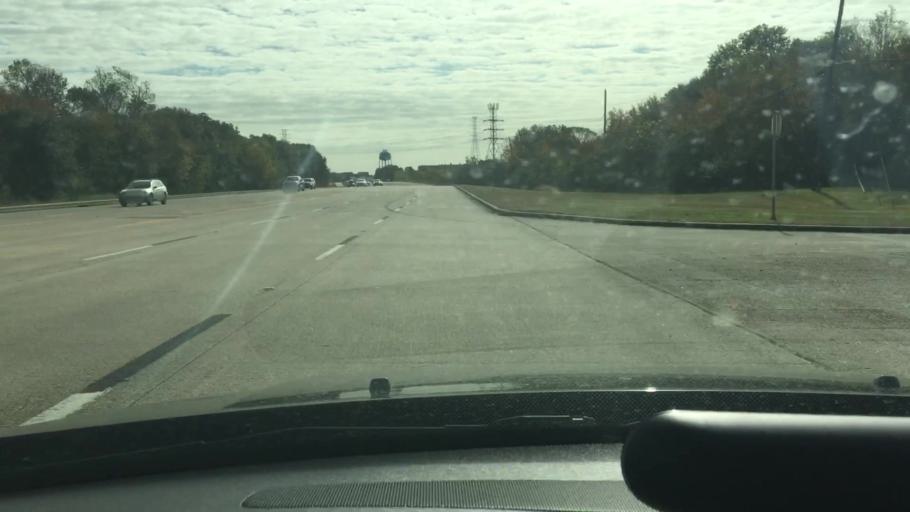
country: US
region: Texas
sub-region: Harris County
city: Nassau Bay
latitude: 29.5314
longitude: -95.0928
